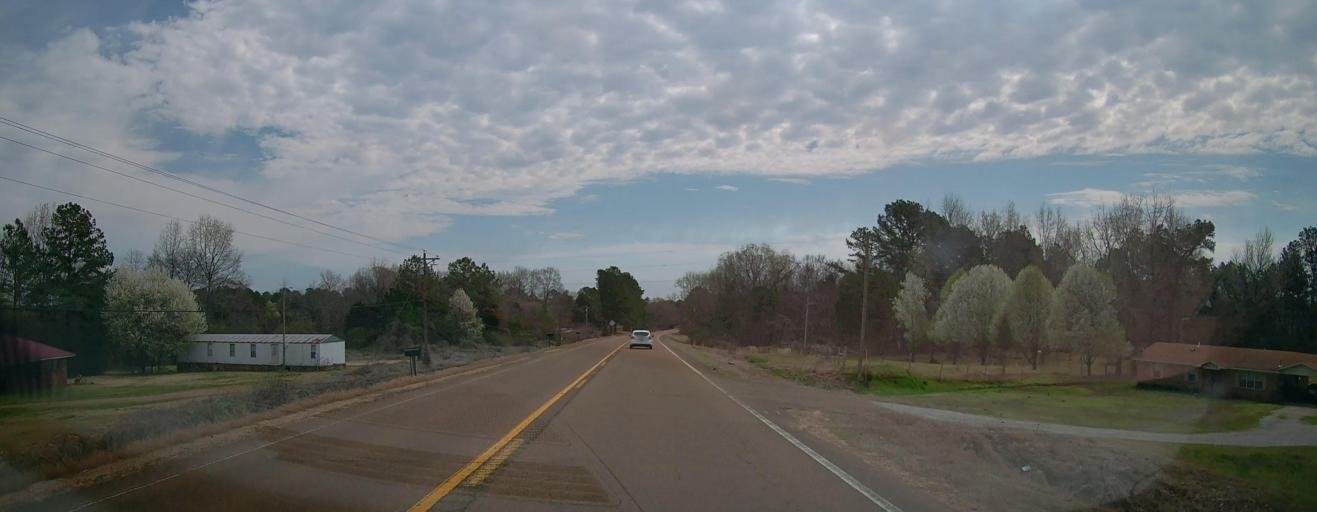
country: US
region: Mississippi
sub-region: Marshall County
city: Holly Springs
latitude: 34.8153
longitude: -89.5269
